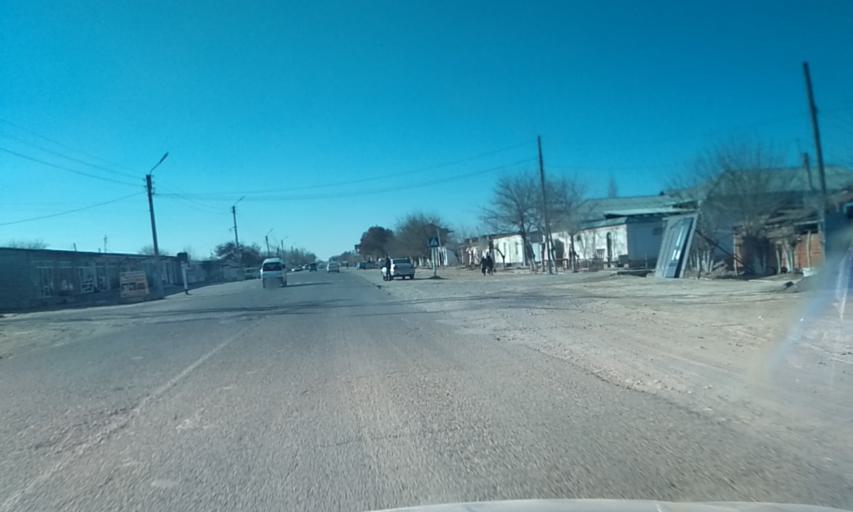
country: UZ
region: Sirdaryo
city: Guliston
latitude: 40.4937
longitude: 68.8091
